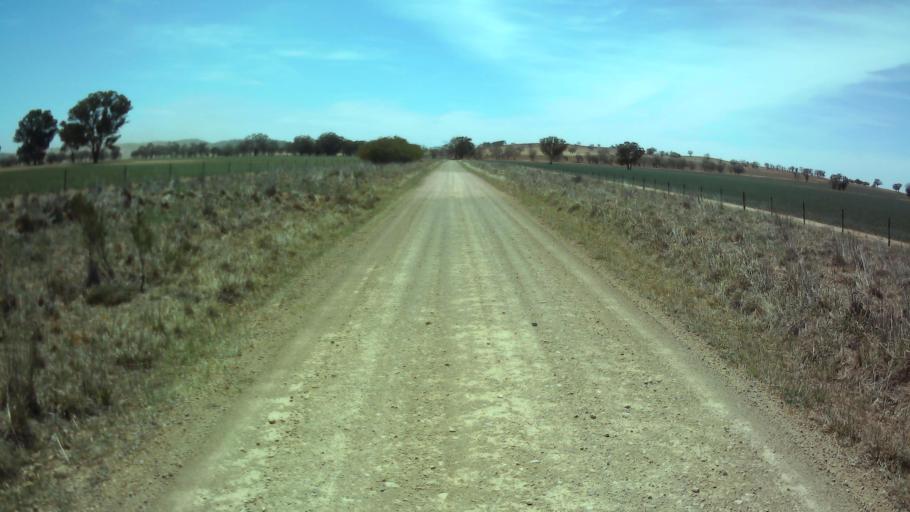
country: AU
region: New South Wales
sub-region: Weddin
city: Grenfell
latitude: -33.9923
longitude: 148.1518
